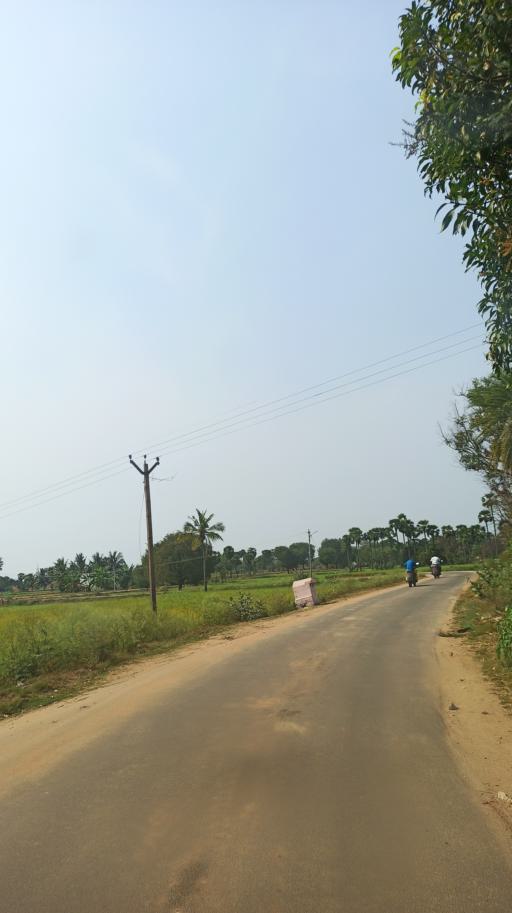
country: IN
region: Tamil Nadu
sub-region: Tiruvannamalai
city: Desur
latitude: 12.4547
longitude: 79.3728
